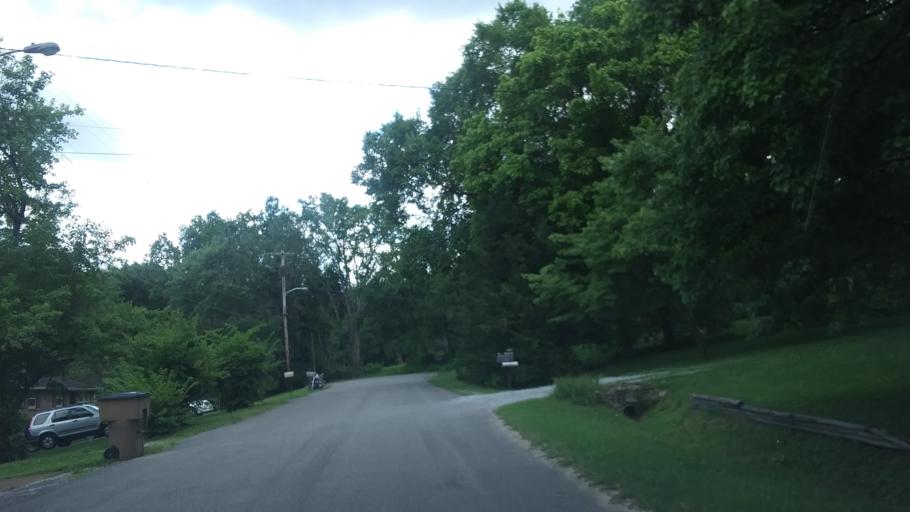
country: US
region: Tennessee
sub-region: Davidson County
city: Oak Hill
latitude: 36.0672
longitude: -86.7028
